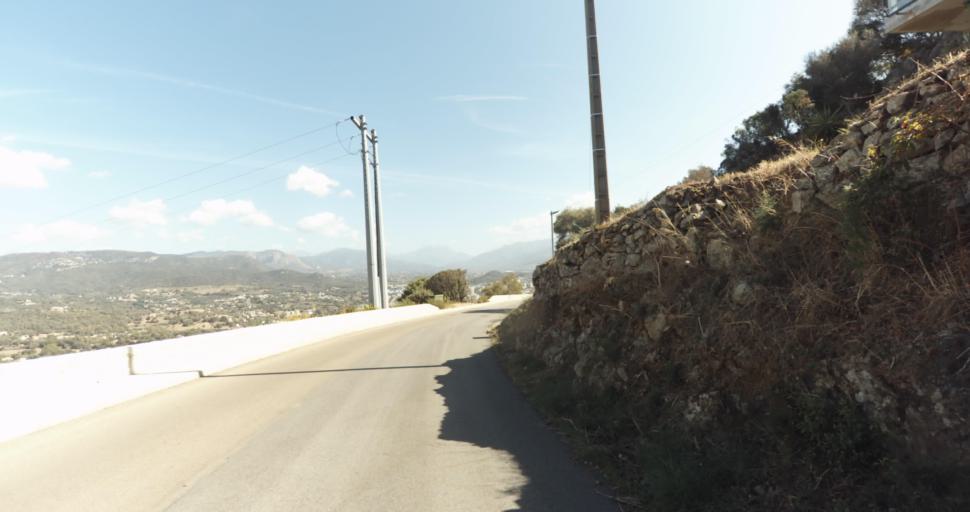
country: FR
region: Corsica
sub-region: Departement de la Corse-du-Sud
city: Ajaccio
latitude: 41.9249
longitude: 8.7224
